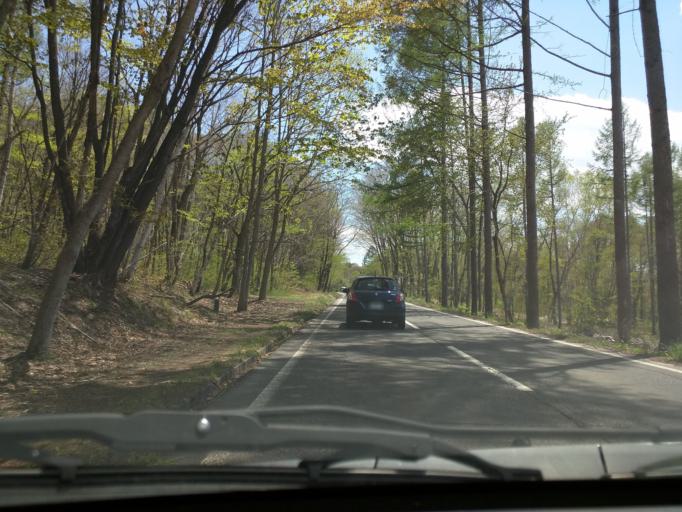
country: JP
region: Nagano
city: Nagano-shi
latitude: 36.7200
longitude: 138.0972
